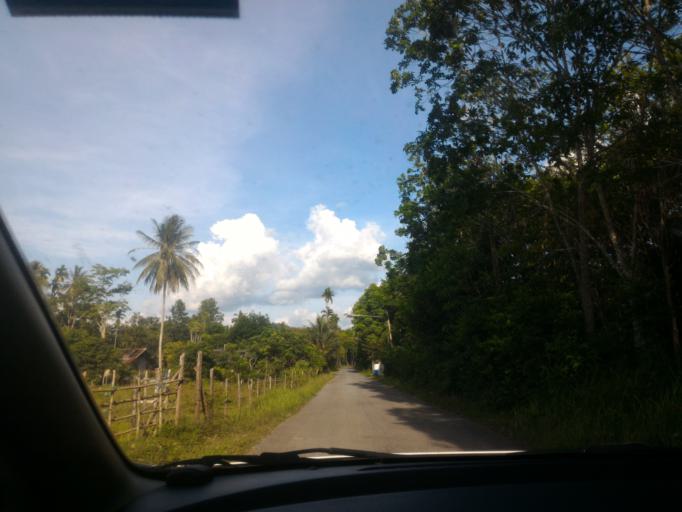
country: TH
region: Nakhon Si Thammarat
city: Thung Song
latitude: 8.1151
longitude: 99.6546
